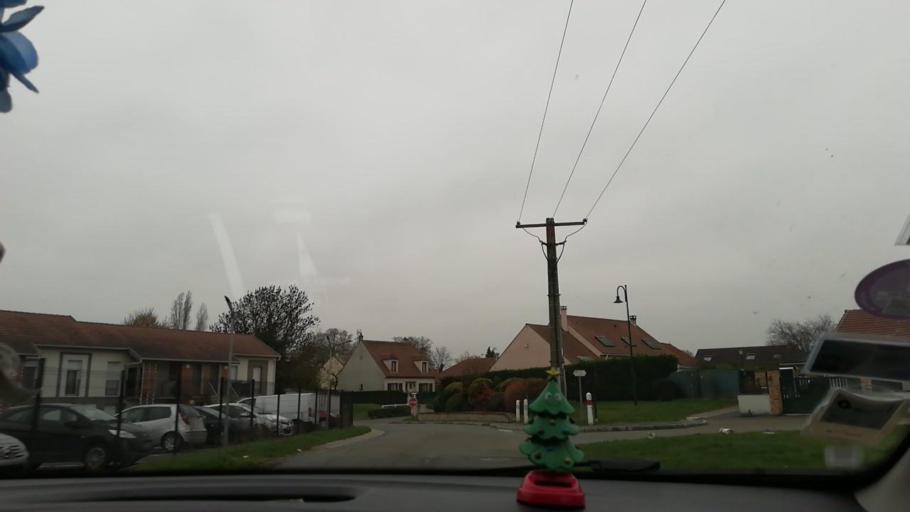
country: FR
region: Ile-de-France
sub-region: Departement de Seine-et-Marne
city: Charny
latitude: 48.9734
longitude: 2.7641
